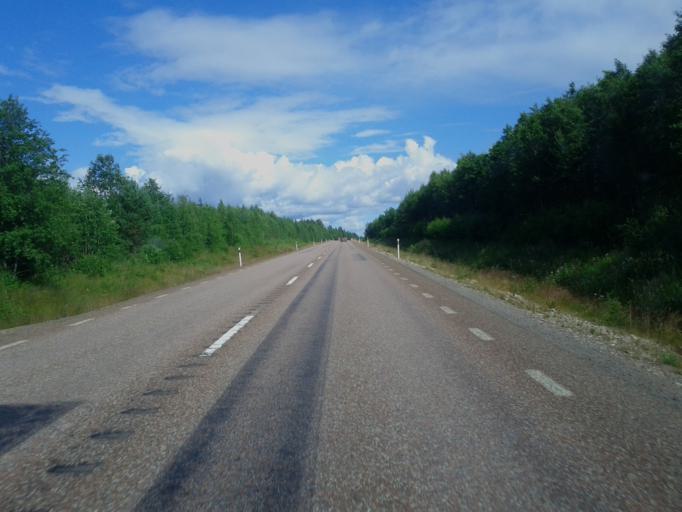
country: SE
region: Dalarna
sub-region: Rattviks Kommun
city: Raettvik
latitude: 60.8450
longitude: 15.1721
